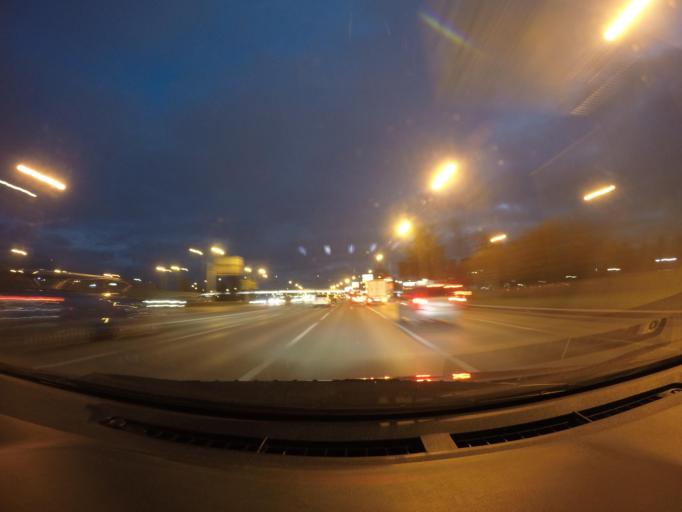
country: RU
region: Moskovskaya
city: Razvilka
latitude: 55.5952
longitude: 37.7264
